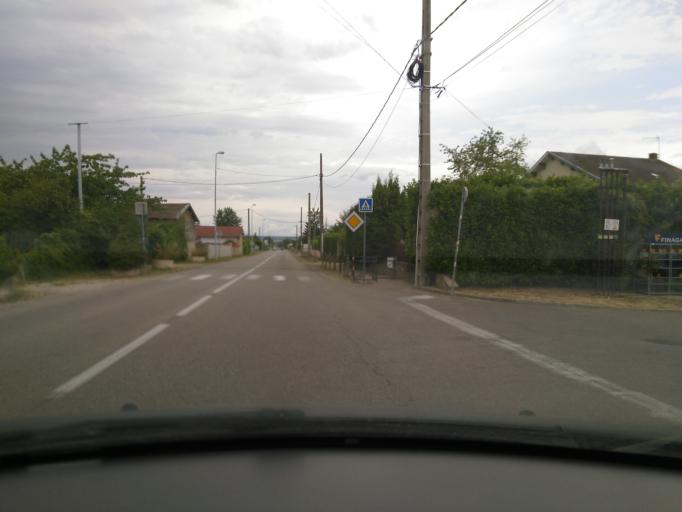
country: FR
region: Rhone-Alpes
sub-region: Departement de l'Isere
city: Beaurepaire
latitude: 45.3414
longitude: 5.0478
